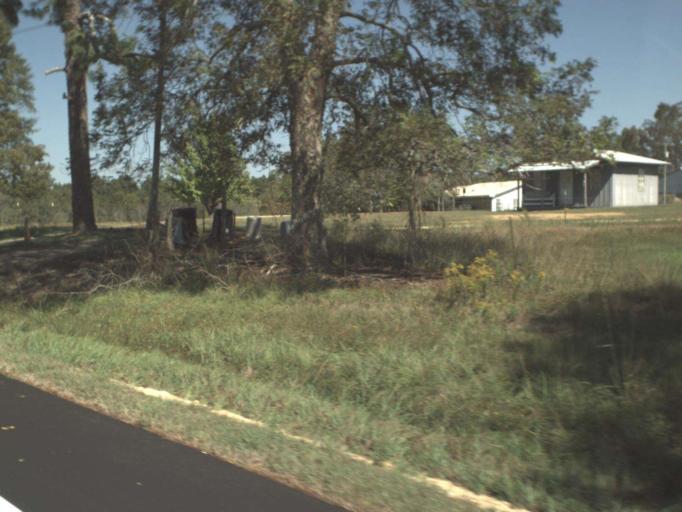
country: US
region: Alabama
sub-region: Covington County
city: Florala
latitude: 30.9336
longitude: -86.2809
